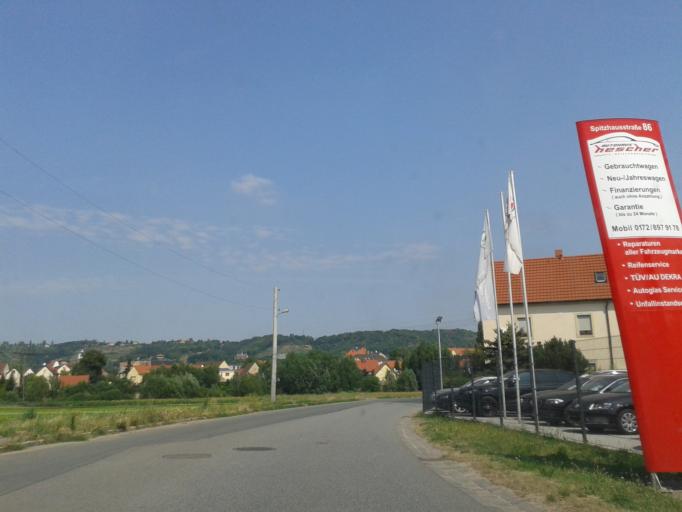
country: DE
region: Saxony
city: Radebeul
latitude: 51.0940
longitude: 13.6747
